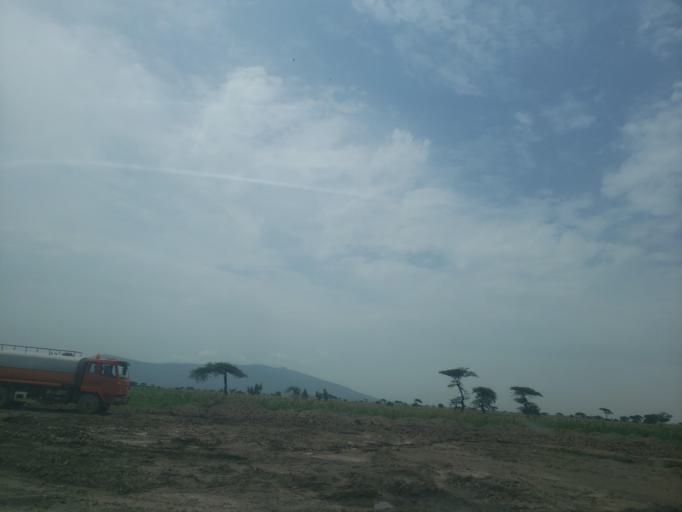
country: ET
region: Oromiya
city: Ziway
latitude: 7.8400
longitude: 38.6566
